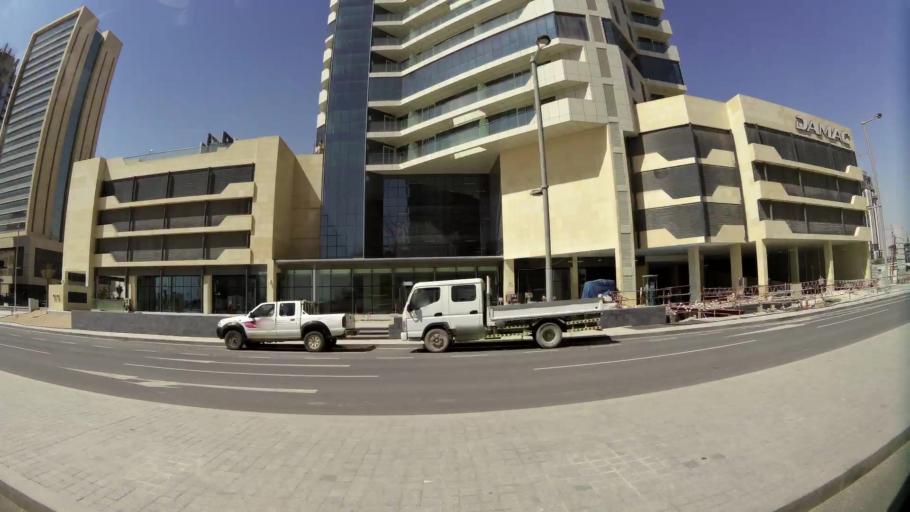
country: QA
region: Baladiyat ad Dawhah
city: Doha
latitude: 25.3908
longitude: 51.5228
